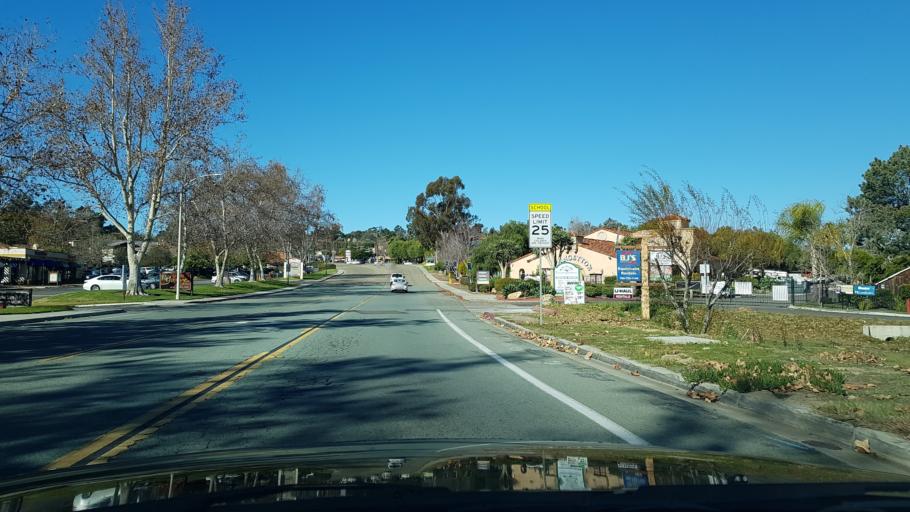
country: US
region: California
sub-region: San Diego County
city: Rancho Santa Fe
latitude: 33.0348
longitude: -117.2368
